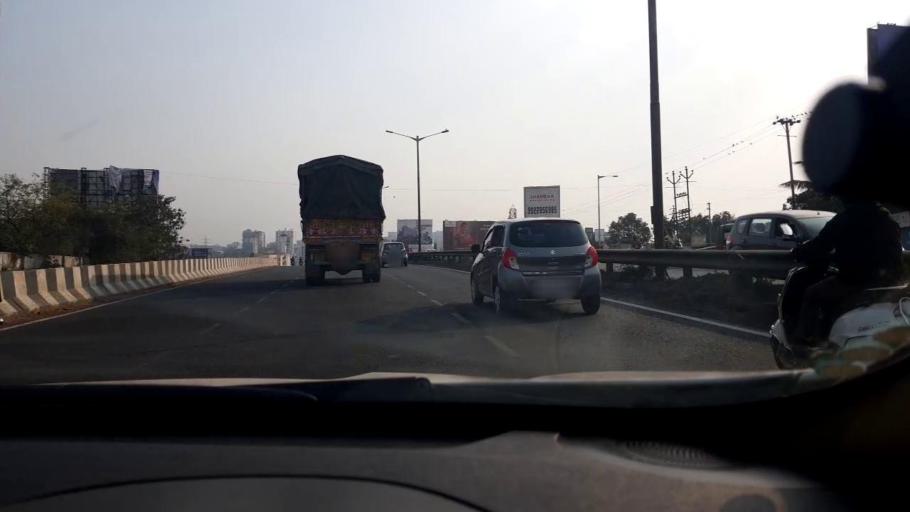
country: IN
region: Maharashtra
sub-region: Pune Division
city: Kharakvasla
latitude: 18.5176
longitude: 73.7689
